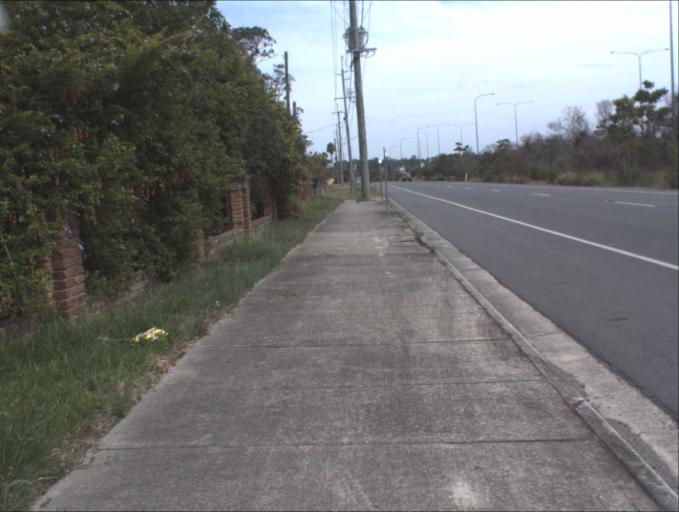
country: AU
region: Queensland
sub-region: Logan
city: Beenleigh
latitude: -27.6895
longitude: 153.1921
